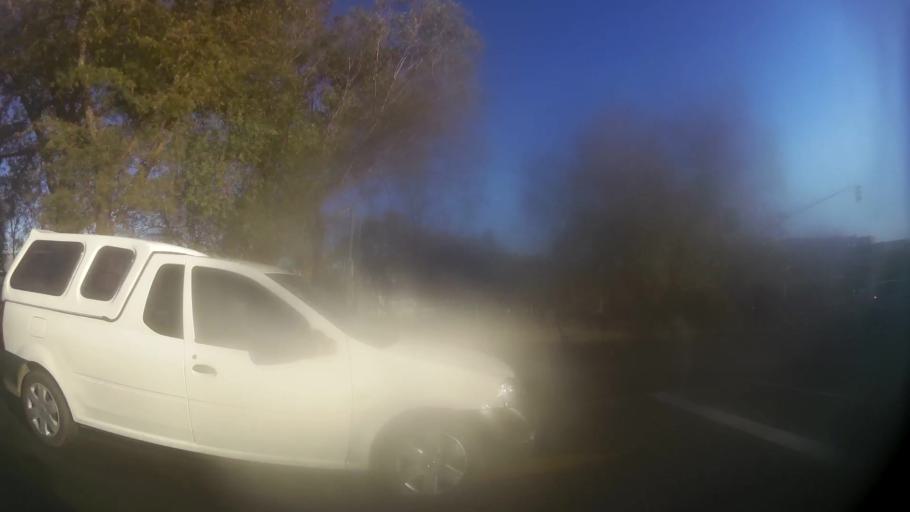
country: ZA
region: Gauteng
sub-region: City of Johannesburg Metropolitan Municipality
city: Midrand
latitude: -25.9992
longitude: 28.1262
